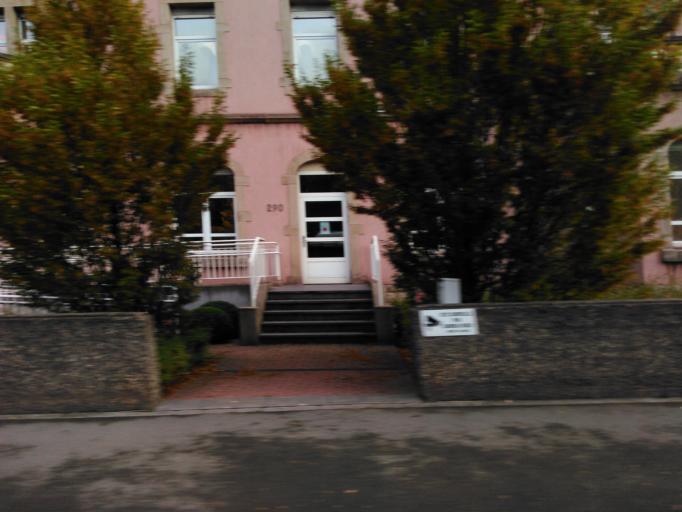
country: LU
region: Luxembourg
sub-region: Canton d'Esch-sur-Alzette
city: Esch-sur-Alzette
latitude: 49.5056
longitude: 5.9604
